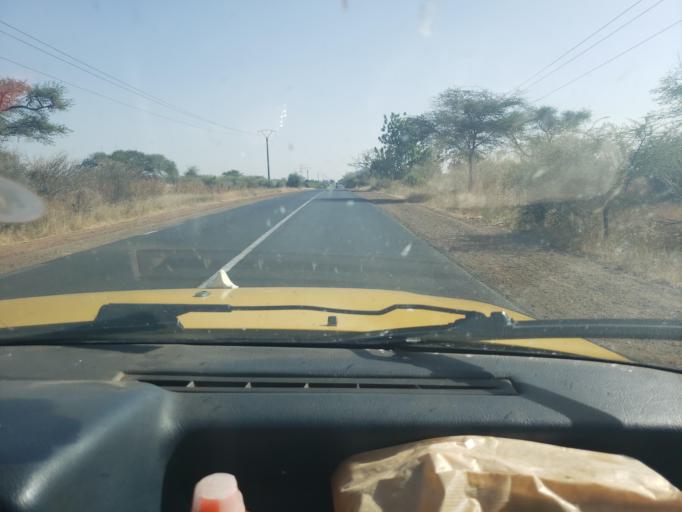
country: SN
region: Louga
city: Louga
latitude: 15.6621
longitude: -16.2582
